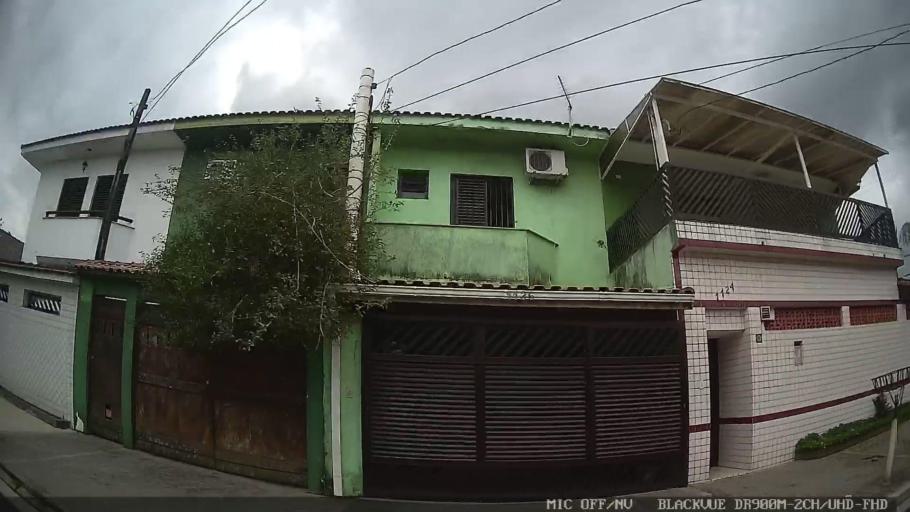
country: BR
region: Sao Paulo
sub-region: Guaruja
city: Guaruja
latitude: -23.9940
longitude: -46.2818
